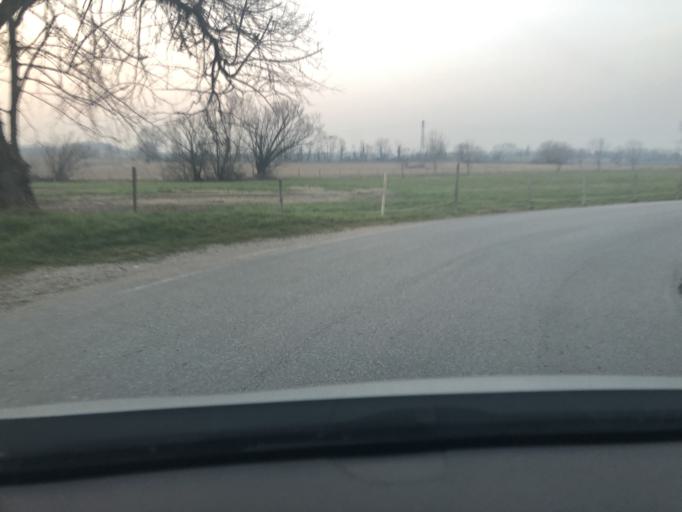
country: IT
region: Veneto
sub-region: Provincia di Verona
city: San Giorgio in Salici
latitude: 45.3926
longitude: 10.7986
